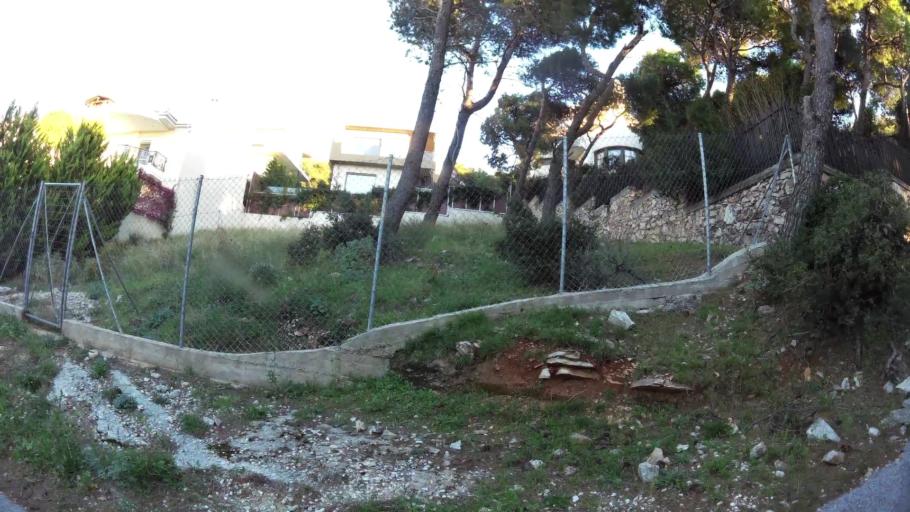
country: GR
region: Attica
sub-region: Nomarchia Athinas
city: Penteli
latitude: 38.0490
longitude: 23.8604
